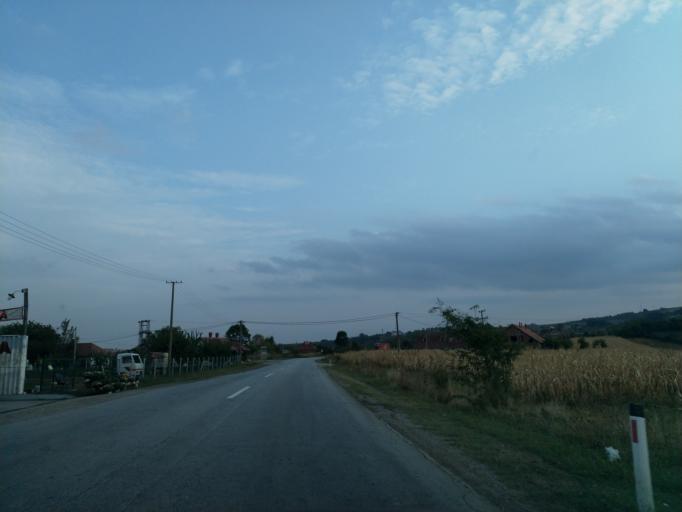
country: RS
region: Central Serbia
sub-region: Sumadijski Okrug
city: Topola
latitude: 44.1830
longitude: 20.7393
